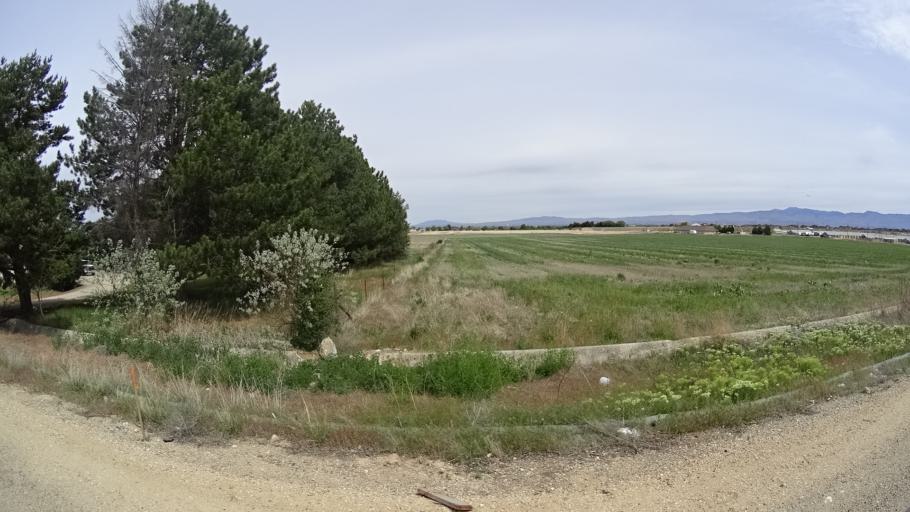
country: US
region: Idaho
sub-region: Ada County
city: Meridian
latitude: 43.5611
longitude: -116.3971
